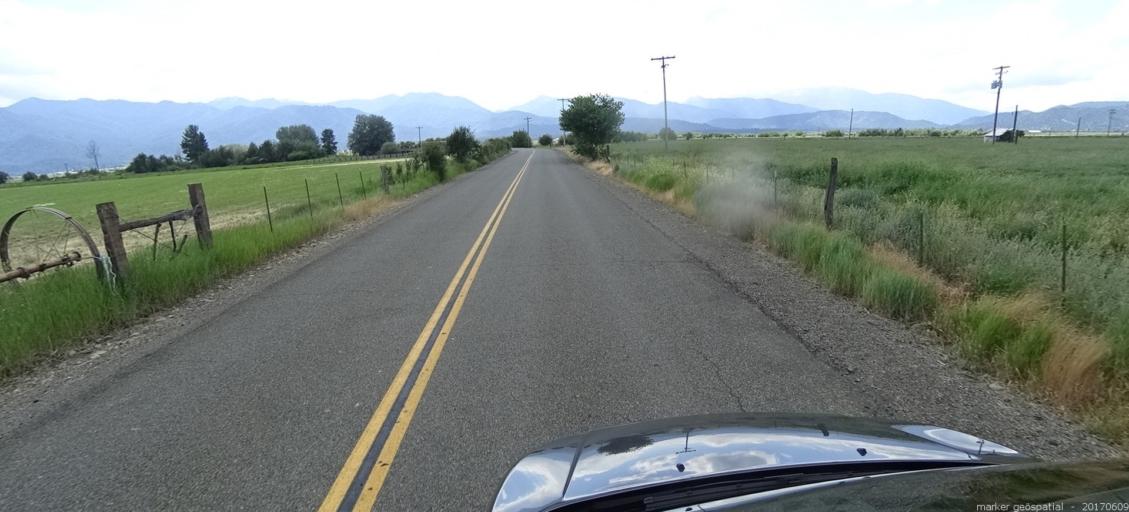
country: US
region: California
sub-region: Siskiyou County
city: Yreka
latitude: 41.5194
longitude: -122.8590
